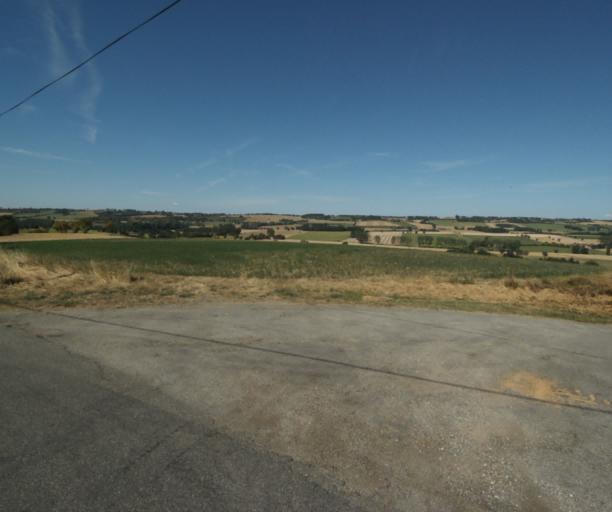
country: FR
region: Midi-Pyrenees
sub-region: Departement de la Haute-Garonne
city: Saint-Felix-Lauragais
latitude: 43.4968
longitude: 1.8927
